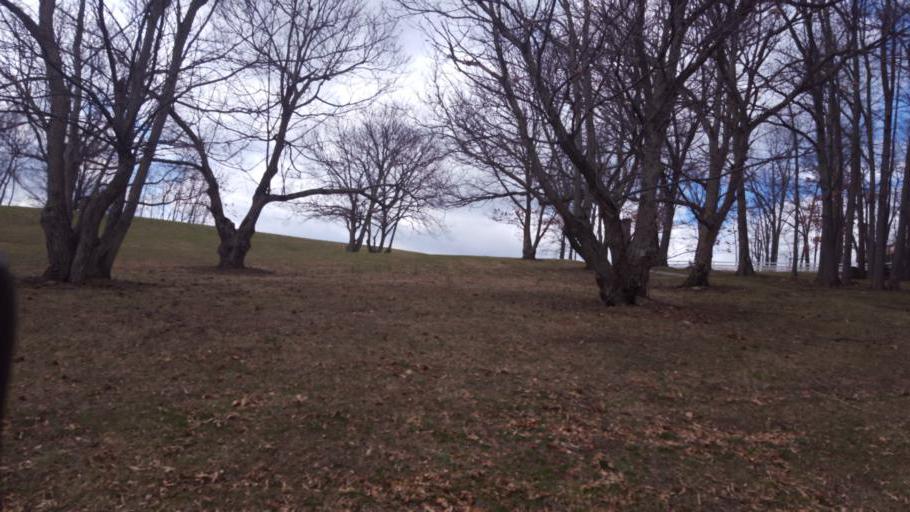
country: US
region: Ohio
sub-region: Sandusky County
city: Bellville
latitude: 40.5770
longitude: -82.4843
